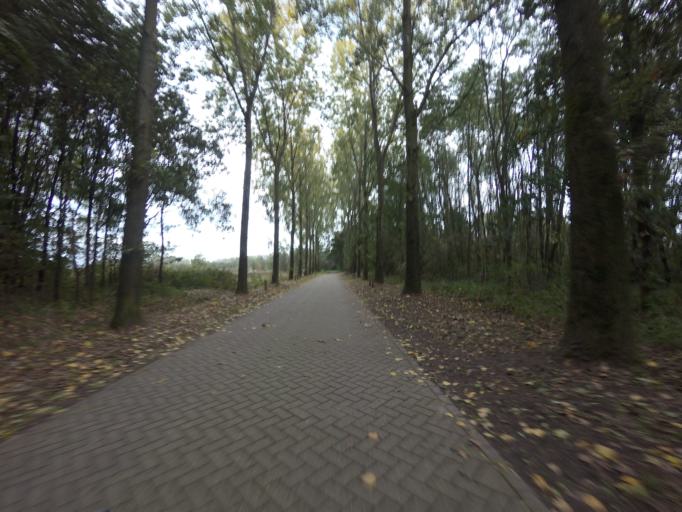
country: NL
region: North Brabant
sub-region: Gemeente Breda
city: Hoge Vucht
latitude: 51.6292
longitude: 4.7503
